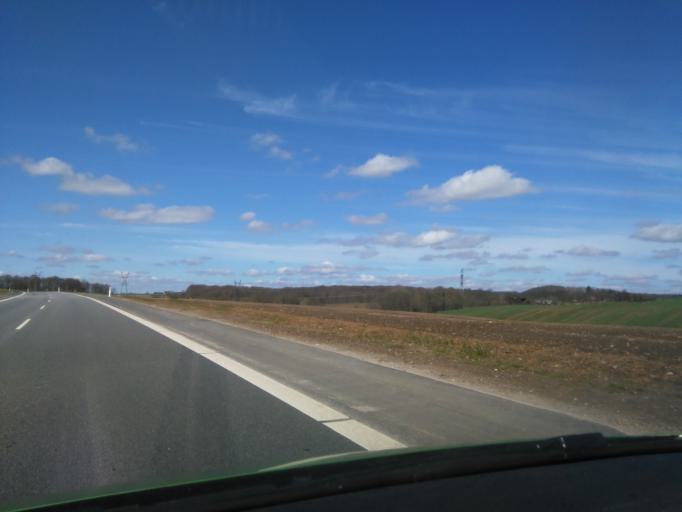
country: DK
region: Central Jutland
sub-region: Odder Kommune
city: Odder
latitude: 55.9827
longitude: 10.1070
